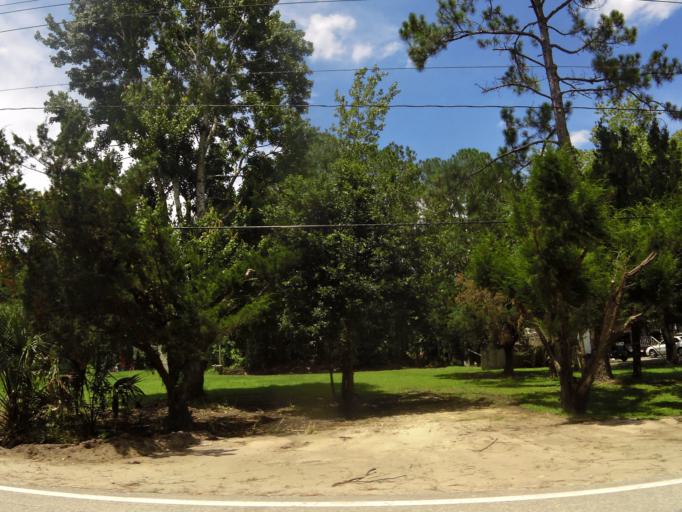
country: US
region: Florida
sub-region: Flagler County
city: Bunnell
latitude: 29.4067
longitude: -81.1949
